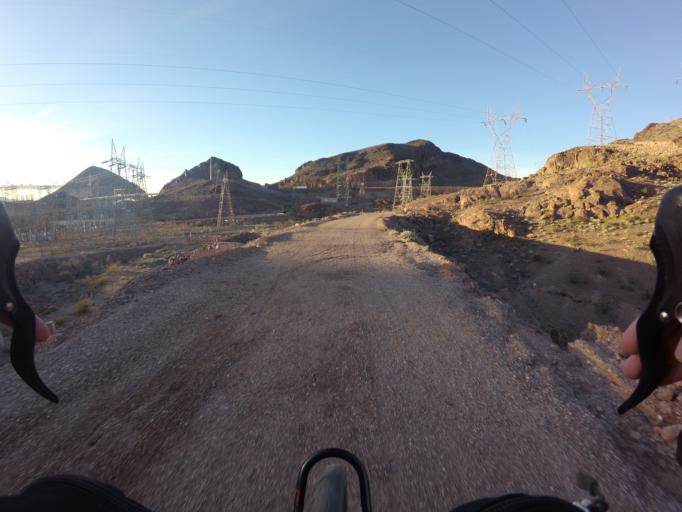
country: US
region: Nevada
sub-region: Clark County
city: Boulder City
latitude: 36.0184
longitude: -114.7453
